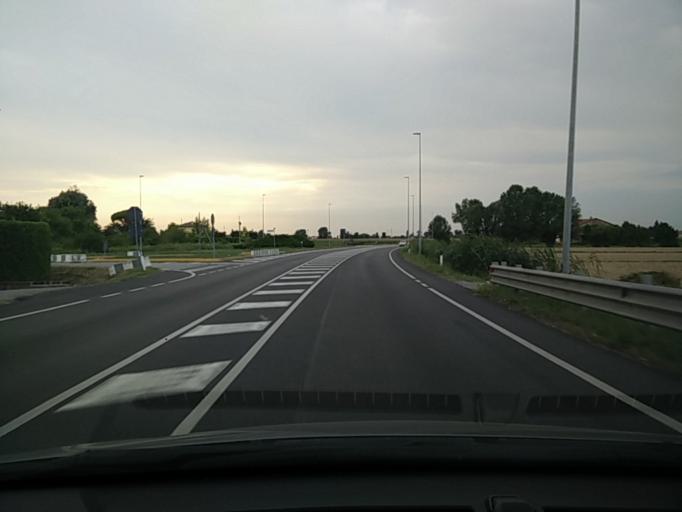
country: IT
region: Veneto
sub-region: Provincia di Venezia
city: Iesolo
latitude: 45.5407
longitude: 12.6215
